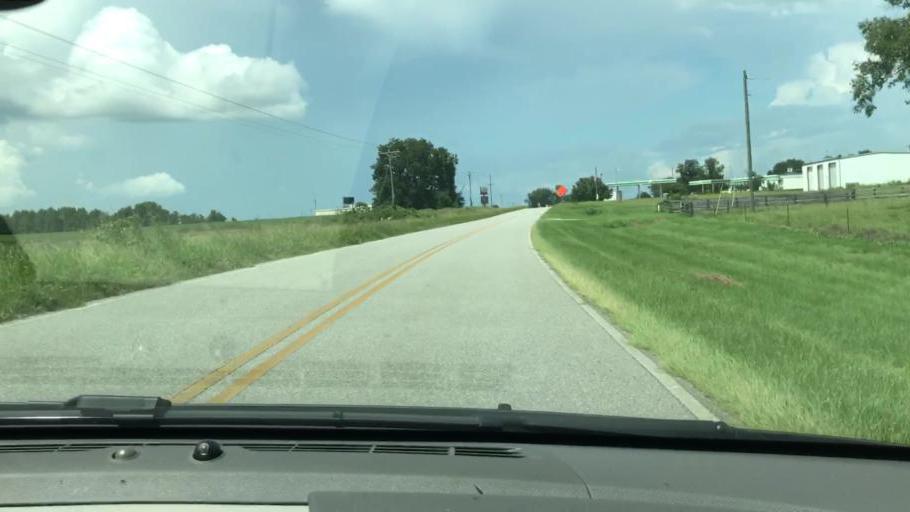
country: US
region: Georgia
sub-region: Seminole County
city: Donalsonville
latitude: 31.0879
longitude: -84.9959
